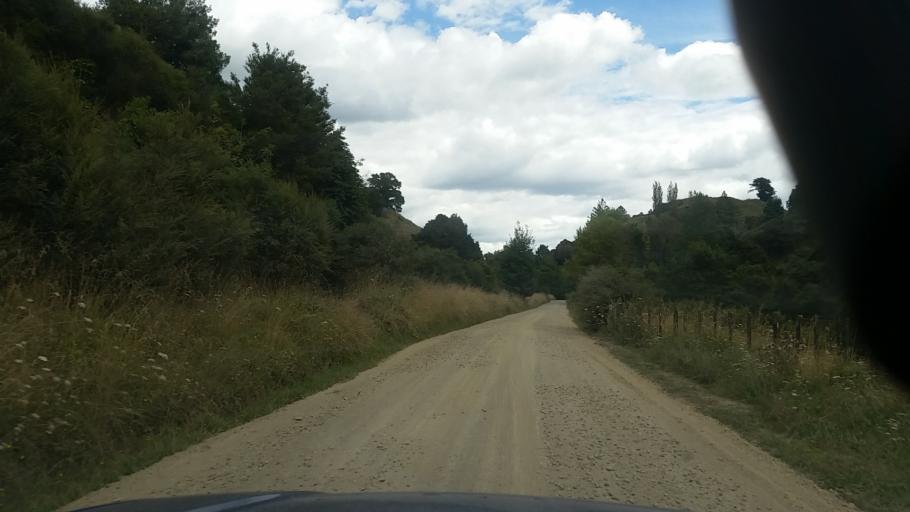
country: NZ
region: Taranaki
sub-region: New Plymouth District
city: Waitara
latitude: -39.0258
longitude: 174.8094
